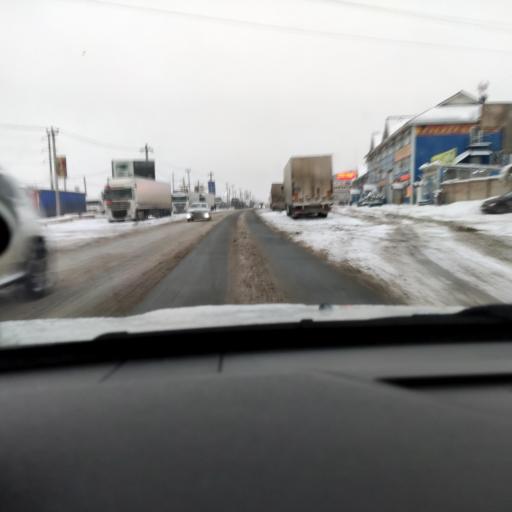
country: RU
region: Samara
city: Smyshlyayevka
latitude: 53.2495
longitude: 50.4745
